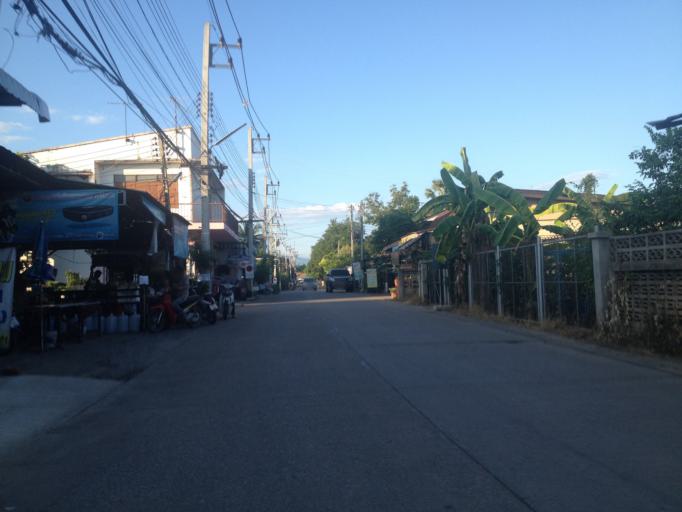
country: TH
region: Chiang Mai
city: San Pa Tong
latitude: 18.6248
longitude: 98.8941
